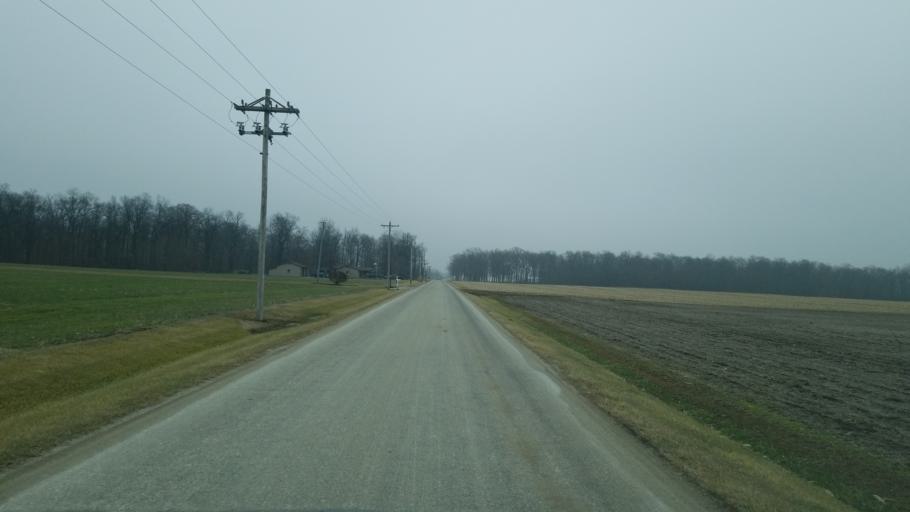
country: US
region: Indiana
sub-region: Adams County
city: Geneva
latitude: 40.5564
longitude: -84.9119
